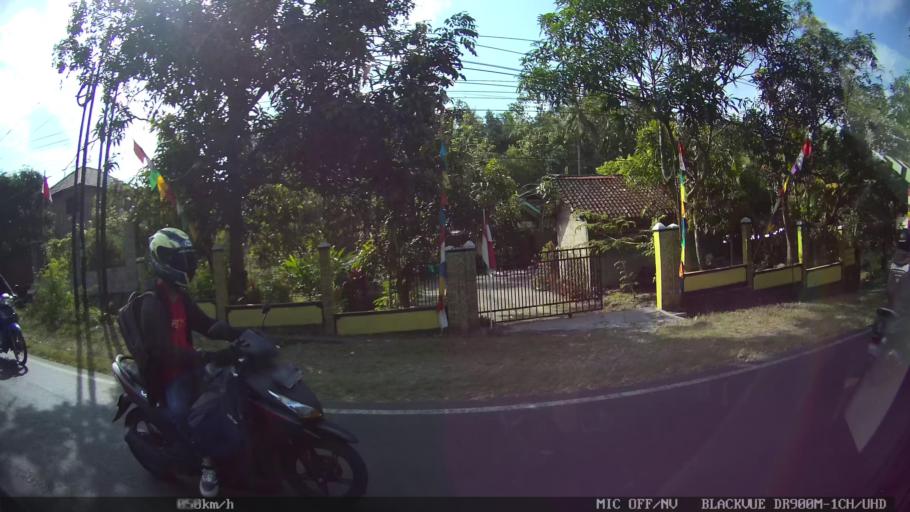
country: ID
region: Daerah Istimewa Yogyakarta
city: Srandakan
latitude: -7.8510
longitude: 110.2170
